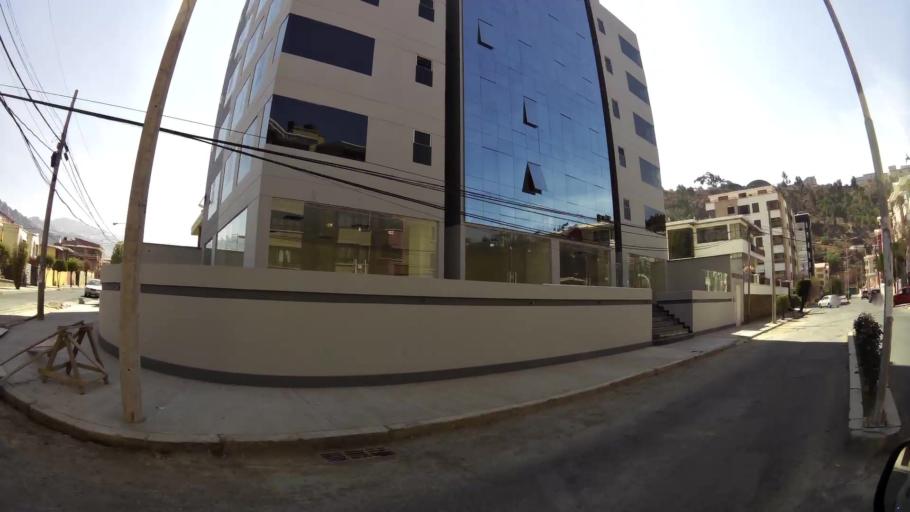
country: BO
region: La Paz
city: La Paz
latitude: -16.5302
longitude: -68.0852
